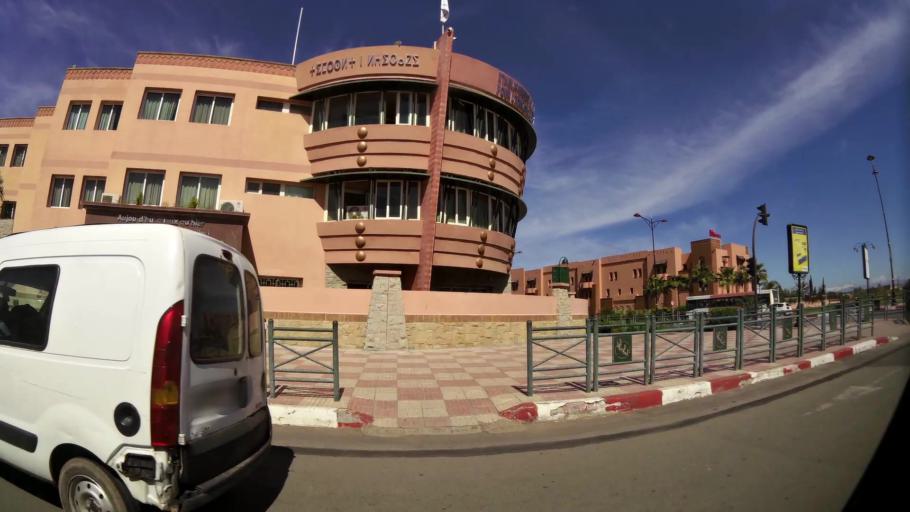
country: MA
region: Marrakech-Tensift-Al Haouz
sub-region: Marrakech
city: Marrakesh
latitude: 31.6783
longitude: -8.0003
